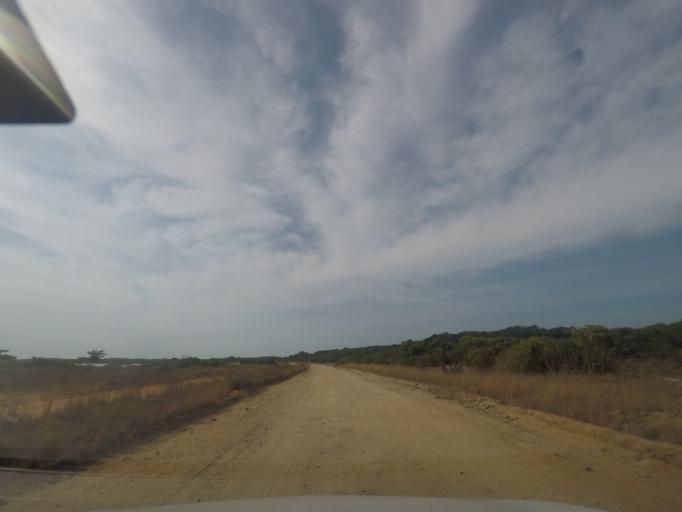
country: BR
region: Rio de Janeiro
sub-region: Marica
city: Marica
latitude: -22.9515
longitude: -42.8859
